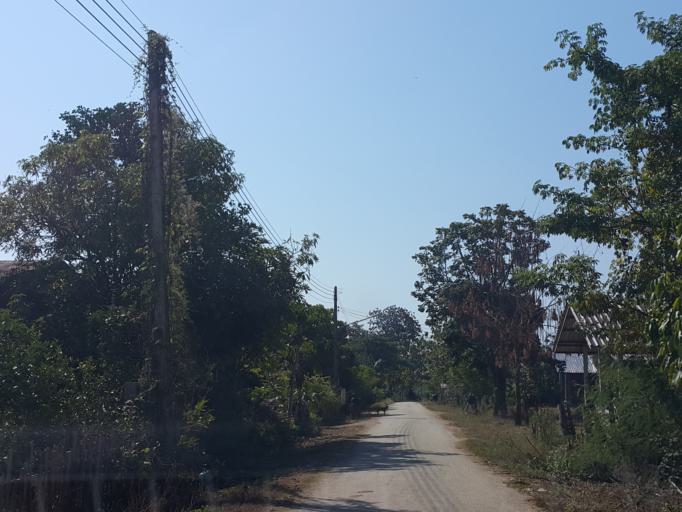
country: TH
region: Sukhothai
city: Thung Saliam
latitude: 17.3423
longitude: 99.4452
